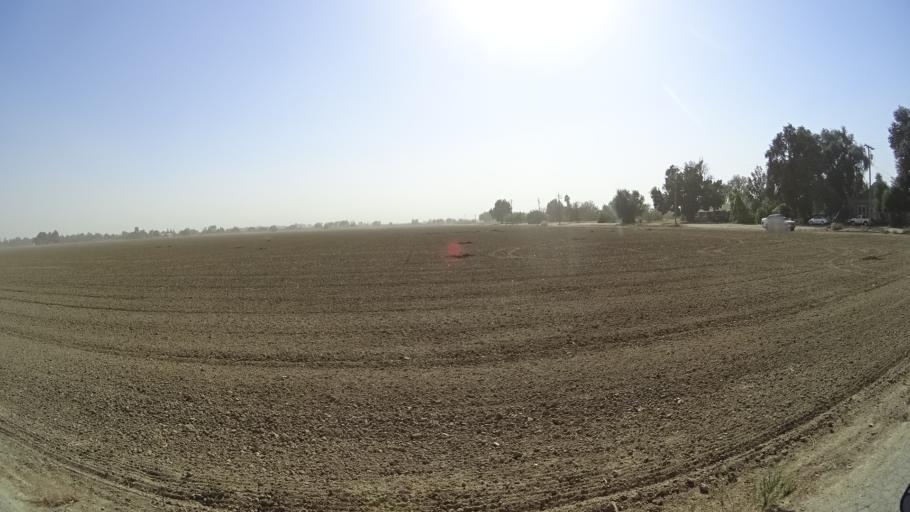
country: US
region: California
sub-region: Yolo County
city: Woodland
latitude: 38.7354
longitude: -121.7806
